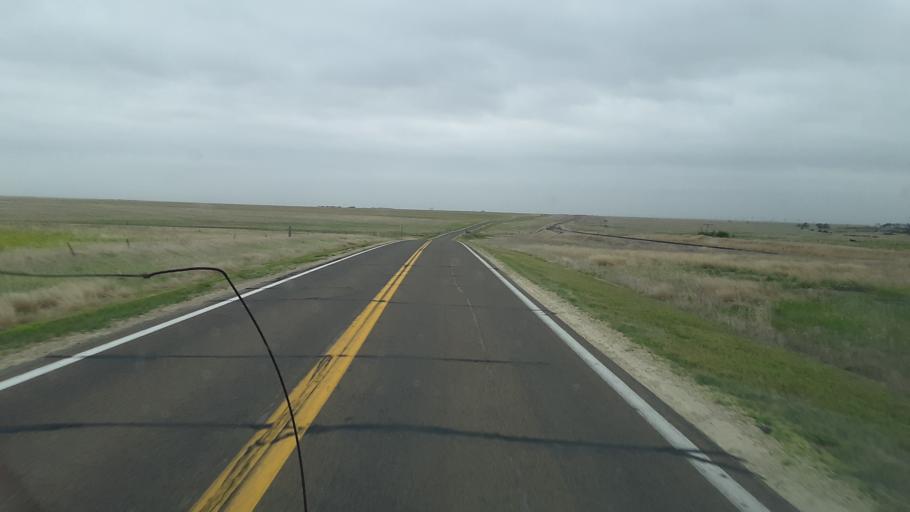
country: US
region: Kansas
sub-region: Logan County
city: Oakley
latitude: 39.1016
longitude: -101.0549
